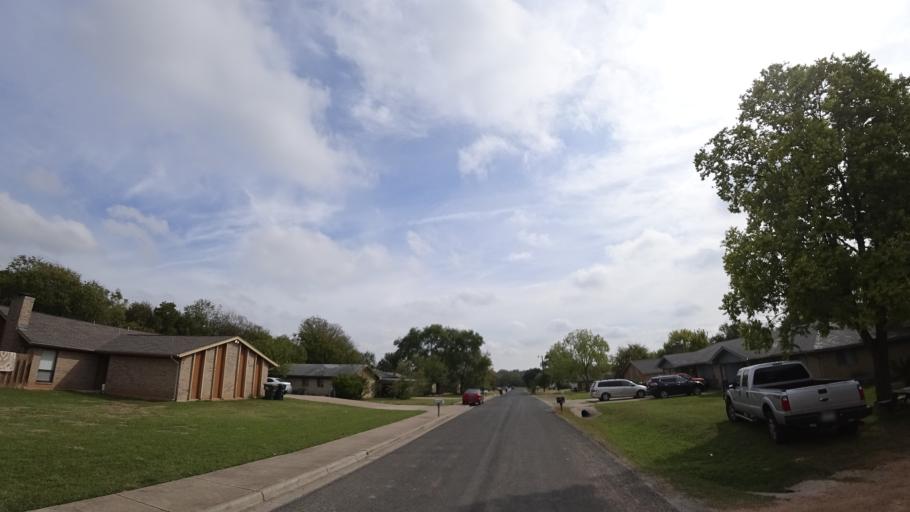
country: US
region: Texas
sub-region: Travis County
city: Wells Branch
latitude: 30.4433
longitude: -97.6625
